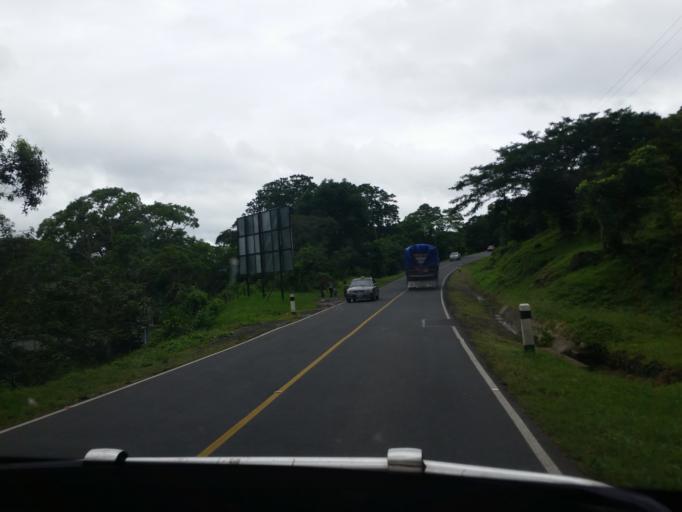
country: NI
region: Jinotega
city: Jinotega
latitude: 13.1150
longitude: -86.0063
